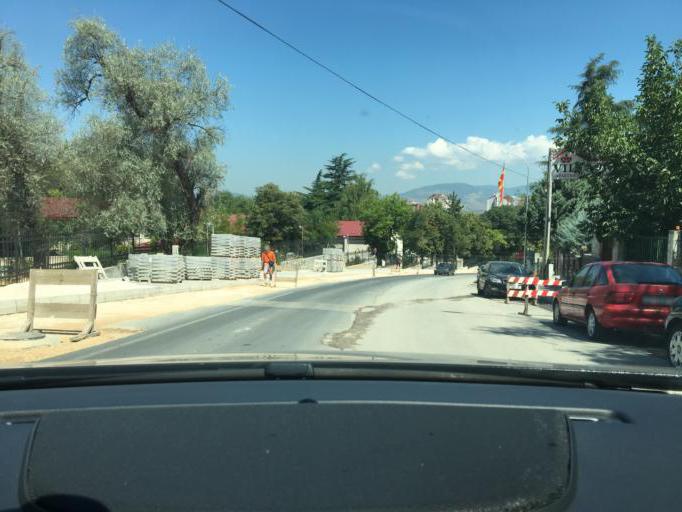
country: MK
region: Karpos
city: Skopje
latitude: 41.9866
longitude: 21.4177
